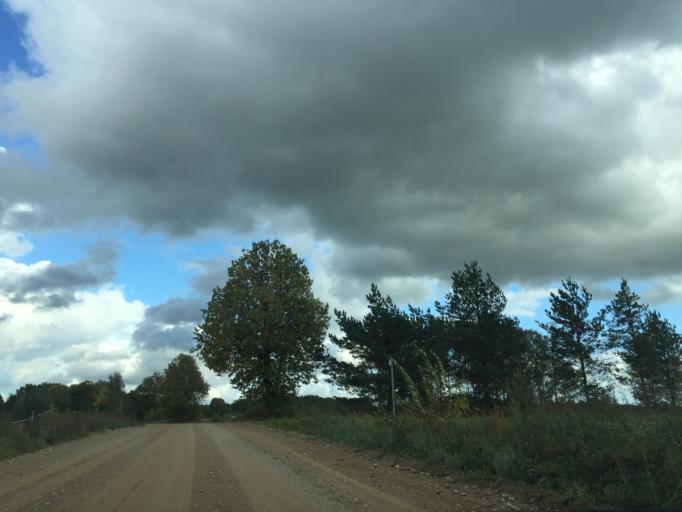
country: LV
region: Malpils
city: Malpils
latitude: 57.0599
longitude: 25.1499
